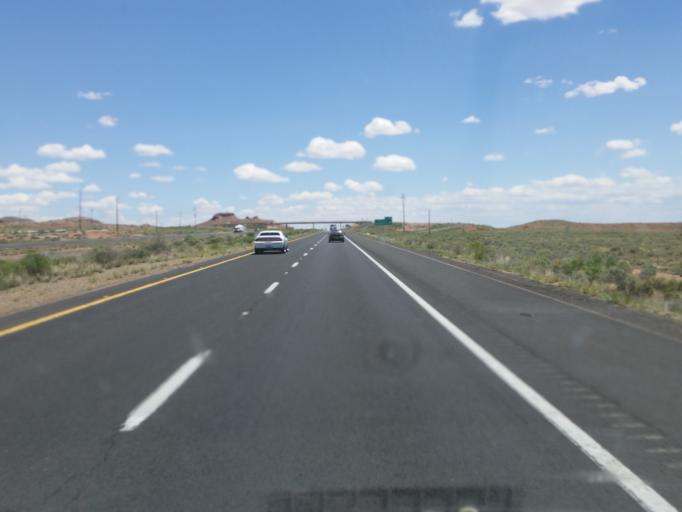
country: US
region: Arizona
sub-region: Navajo County
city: Joseph City
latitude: 34.9264
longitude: -110.2660
